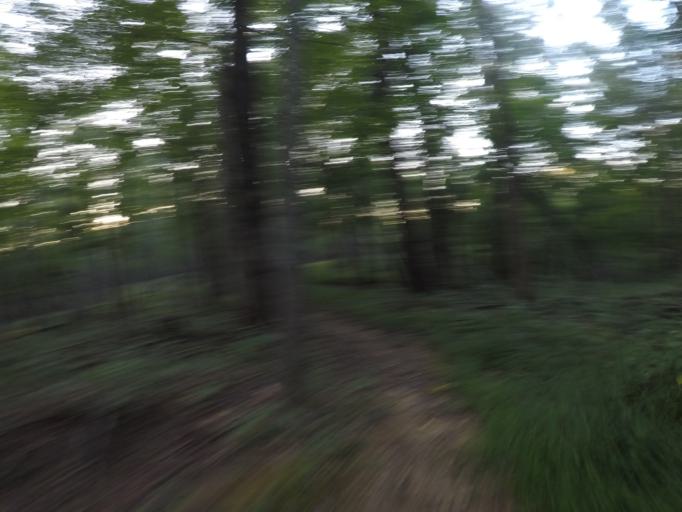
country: US
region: Ohio
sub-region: Lawrence County
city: Ironton
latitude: 38.6090
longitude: -82.6199
